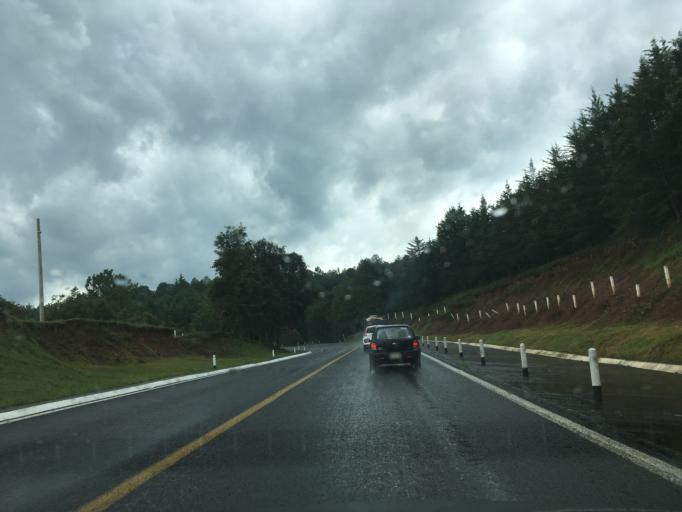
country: MX
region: Michoacan
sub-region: Patzcuaro
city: Santa Ana Chapitiro
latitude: 19.5072
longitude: -101.6946
